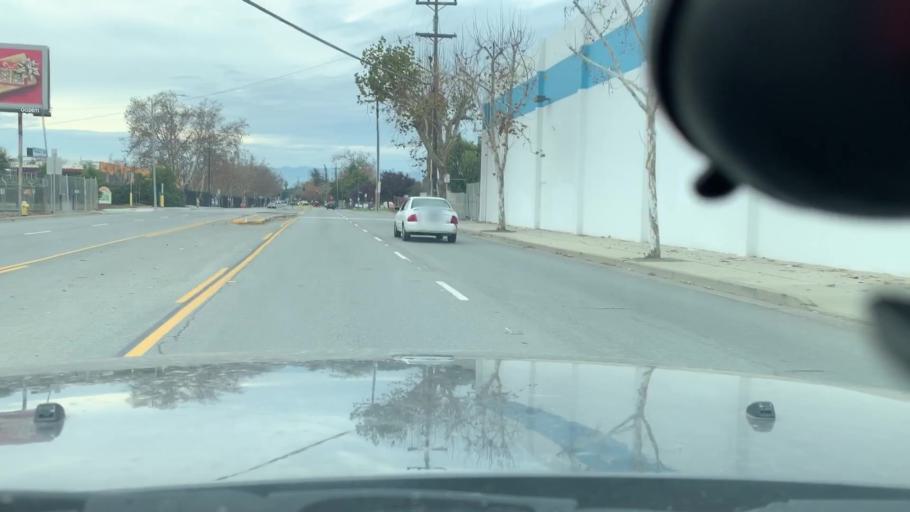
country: US
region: California
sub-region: Santa Clara County
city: San Jose
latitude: 37.3179
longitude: -121.8709
